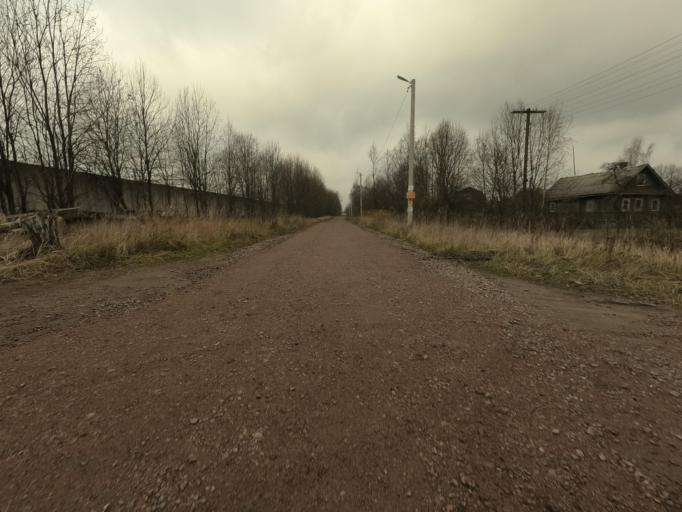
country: RU
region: Leningrad
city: Lyuban'
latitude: 59.4894
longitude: 31.2691
